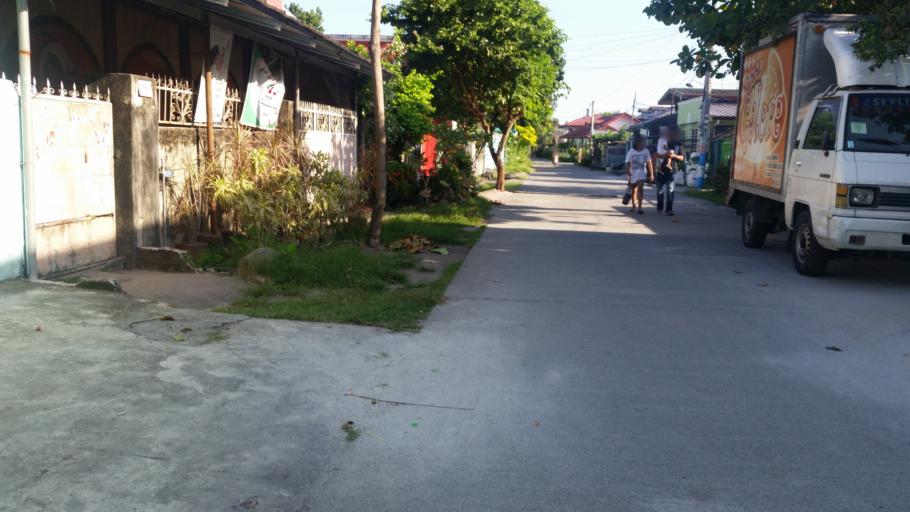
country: PH
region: Central Luzon
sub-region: Province of Pampanga
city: Mabalacat City
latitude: 15.2767
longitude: 120.5684
